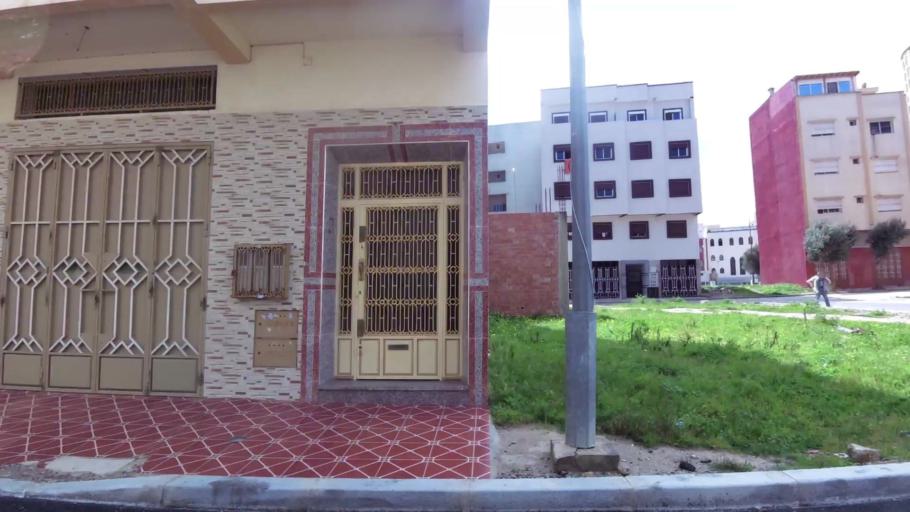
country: MA
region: Tanger-Tetouan
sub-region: Tanger-Assilah
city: Tangier
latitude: 35.7587
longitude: -5.8464
